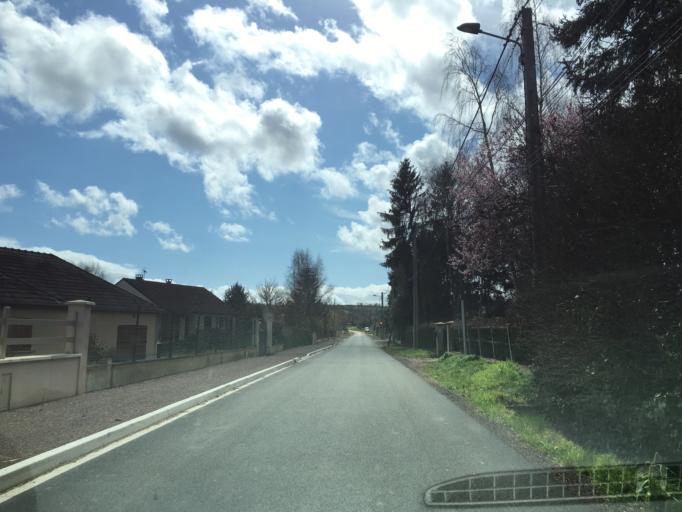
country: FR
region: Bourgogne
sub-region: Departement de l'Yonne
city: Charbuy
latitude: 47.8070
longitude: 3.4195
